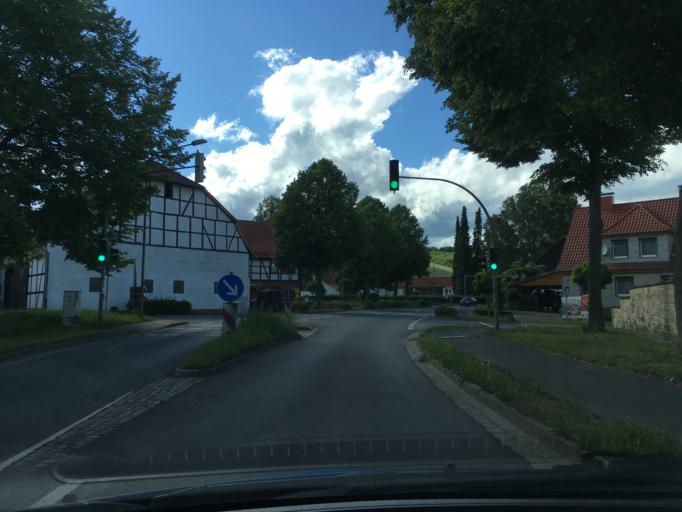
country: DE
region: Lower Saxony
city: Hardegsen
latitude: 51.5975
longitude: 9.8558
